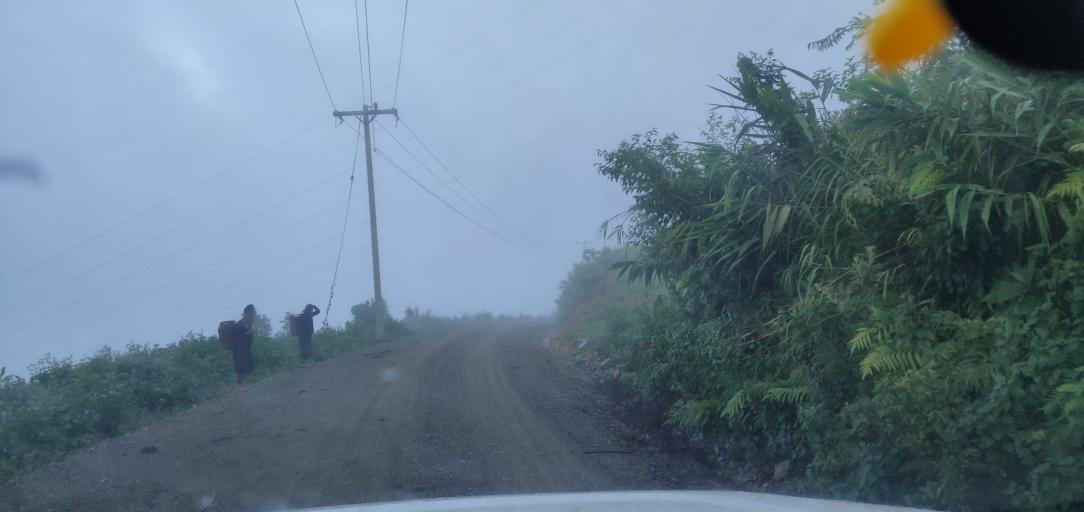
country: LA
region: Phongsali
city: Phongsali
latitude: 21.3979
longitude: 102.2235
